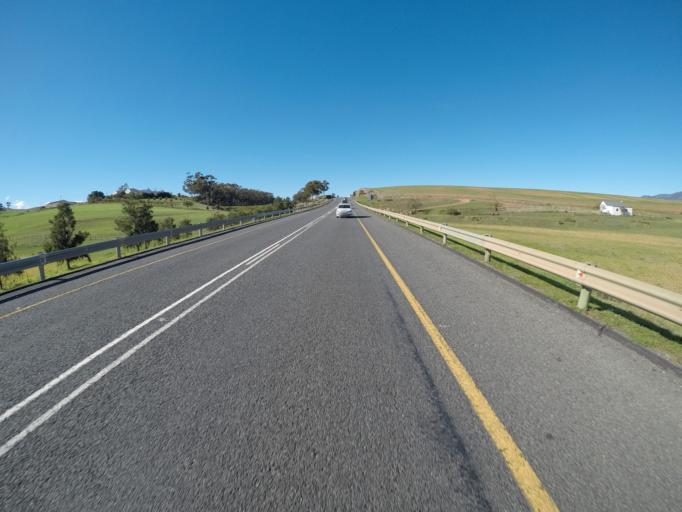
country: ZA
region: Western Cape
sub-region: Overberg District Municipality
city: Hermanus
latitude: -34.2354
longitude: 19.2178
